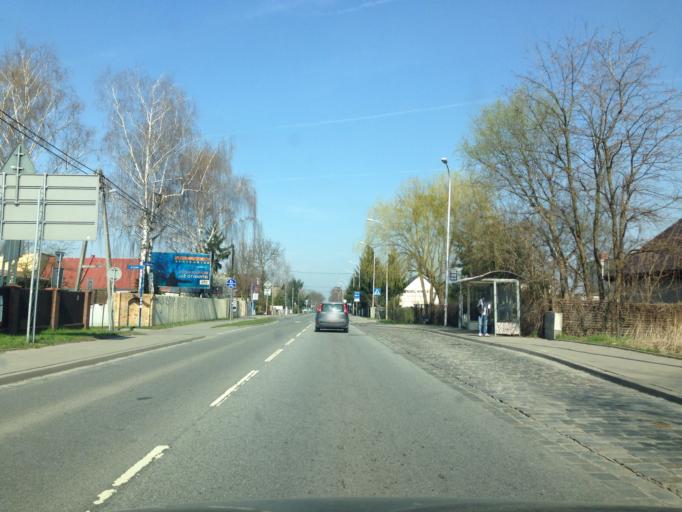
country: PL
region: Lower Silesian Voivodeship
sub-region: Powiat wroclawski
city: Kamieniec Wroclawski
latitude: 51.0969
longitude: 17.1644
